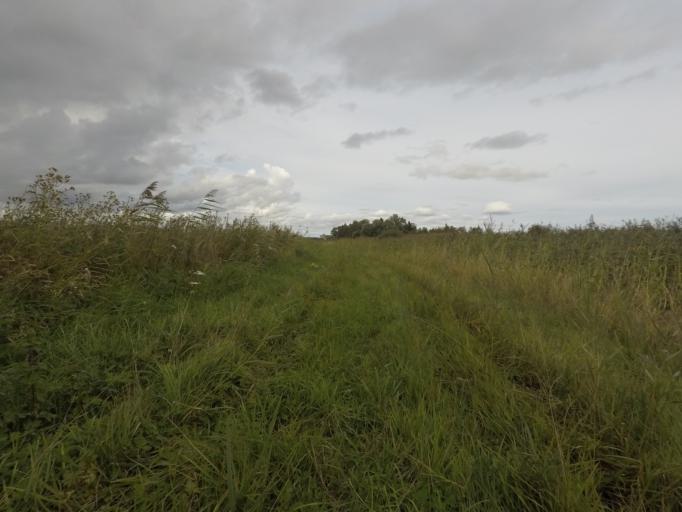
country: SE
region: Vaestmanland
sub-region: Kungsors Kommun
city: Kungsoer
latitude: 59.4604
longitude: 16.0612
